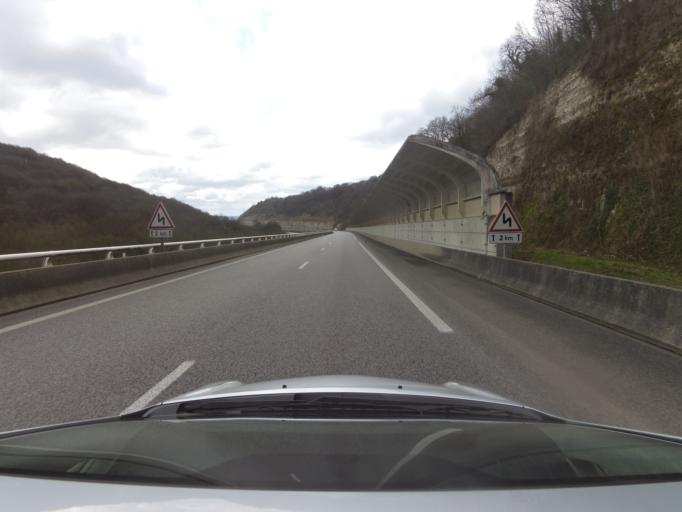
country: FR
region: Haute-Normandie
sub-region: Departement de la Seine-Maritime
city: Rogerville
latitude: 49.5091
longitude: 0.2861
